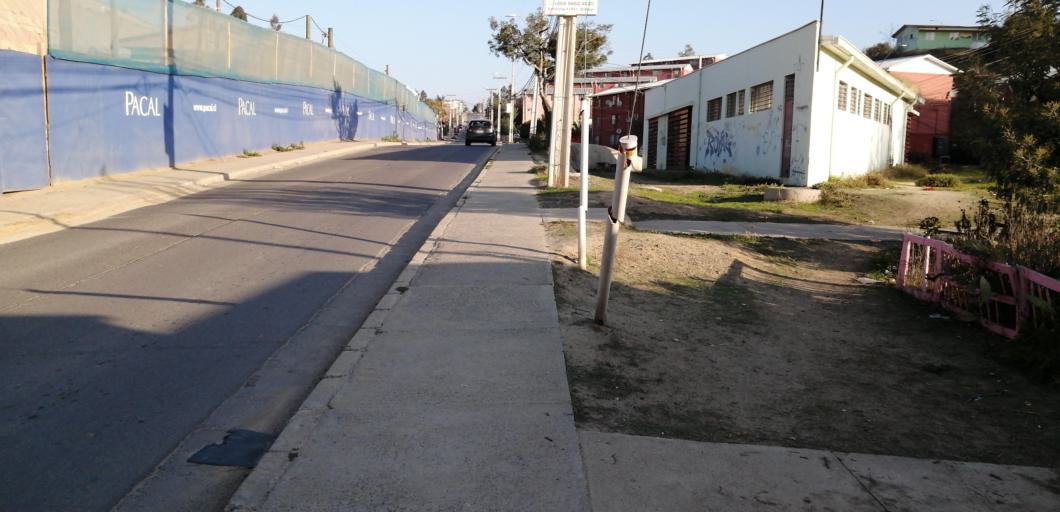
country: CL
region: Valparaiso
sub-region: Provincia de Marga Marga
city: Quilpue
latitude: -33.0571
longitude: -71.4411
